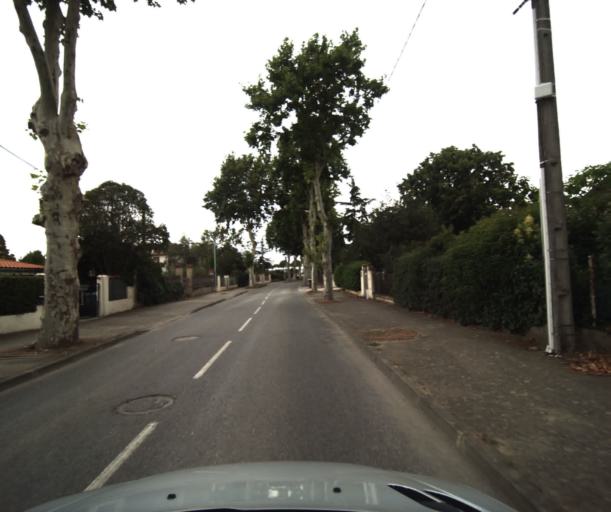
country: FR
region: Midi-Pyrenees
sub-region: Departement de la Haute-Garonne
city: Portet-sur-Garonne
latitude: 43.5285
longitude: 1.3979
